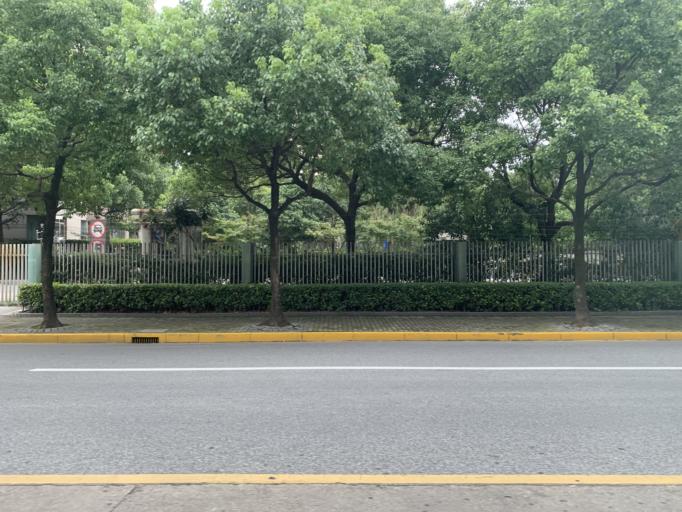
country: CN
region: Shanghai Shi
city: Huamu
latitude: 31.2281
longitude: 121.5619
